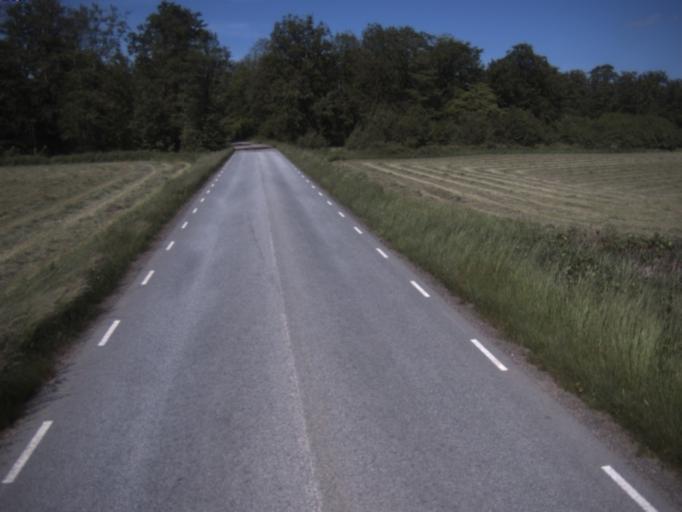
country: SE
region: Skane
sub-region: Helsingborg
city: Odakra
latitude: 56.1126
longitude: 12.6723
